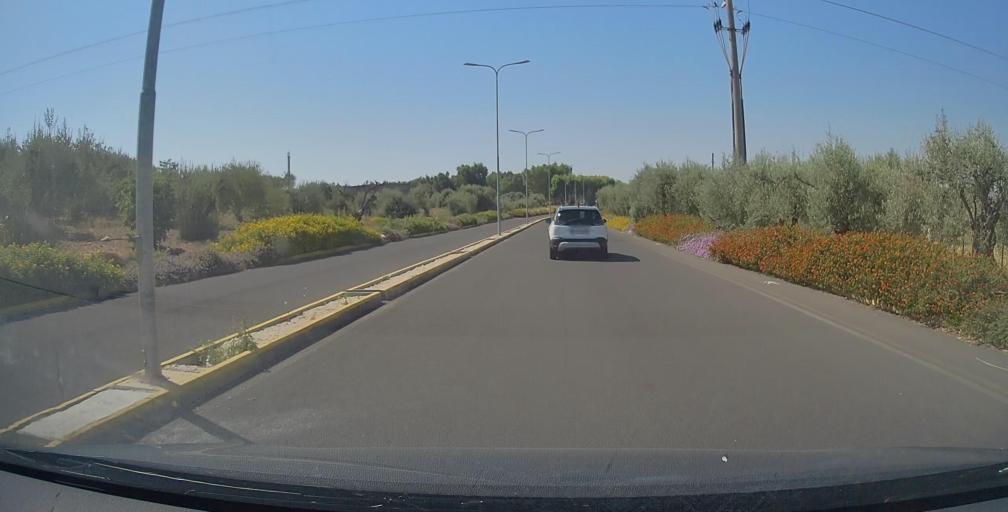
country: IT
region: Sicily
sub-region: Catania
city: Palazzolo
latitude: 37.5405
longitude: 14.9312
